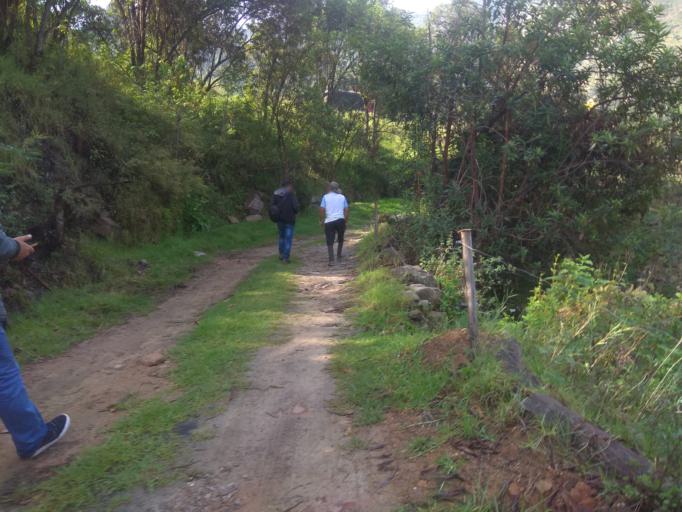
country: CO
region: Boyaca
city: Socha Viejo
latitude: 5.9795
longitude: -72.7041
